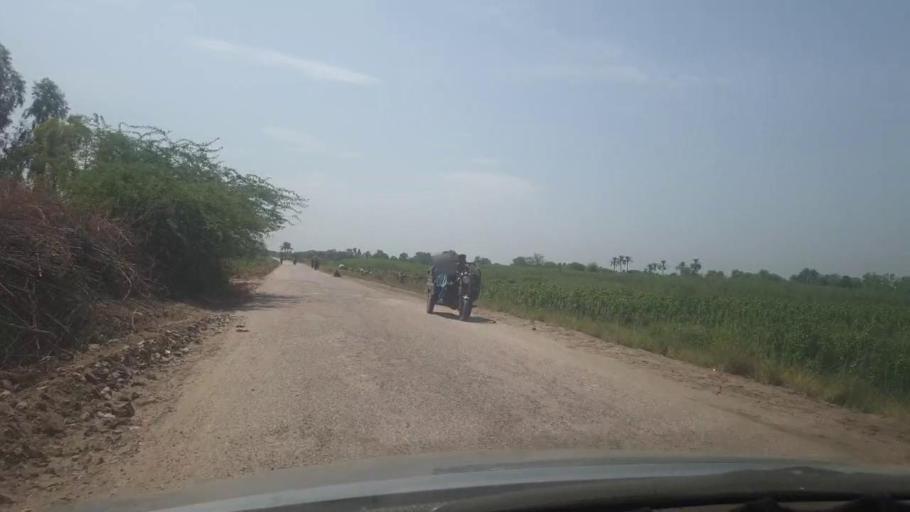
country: PK
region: Sindh
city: Bozdar
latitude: 27.2175
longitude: 68.5698
